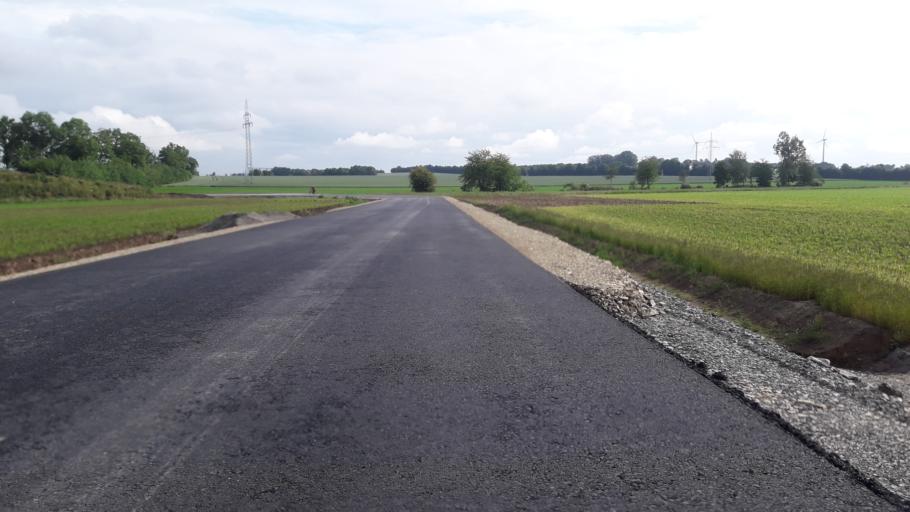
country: DE
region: North Rhine-Westphalia
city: Warburg
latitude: 51.5108
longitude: 9.1404
